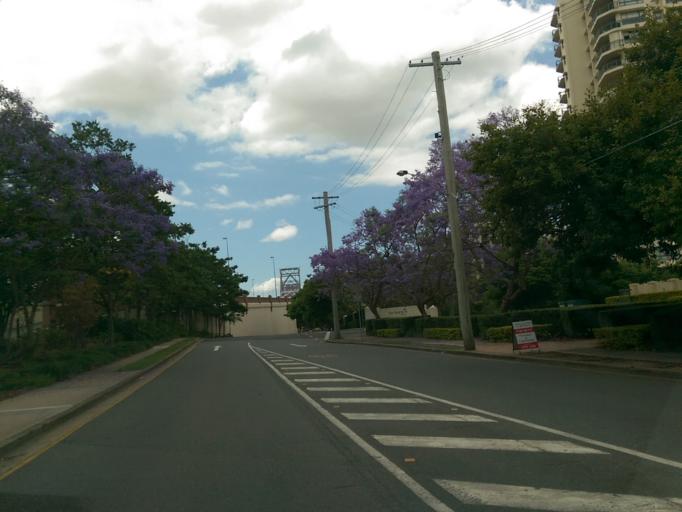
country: AU
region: Queensland
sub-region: Brisbane
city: Brisbane
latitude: -27.4714
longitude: 153.0361
